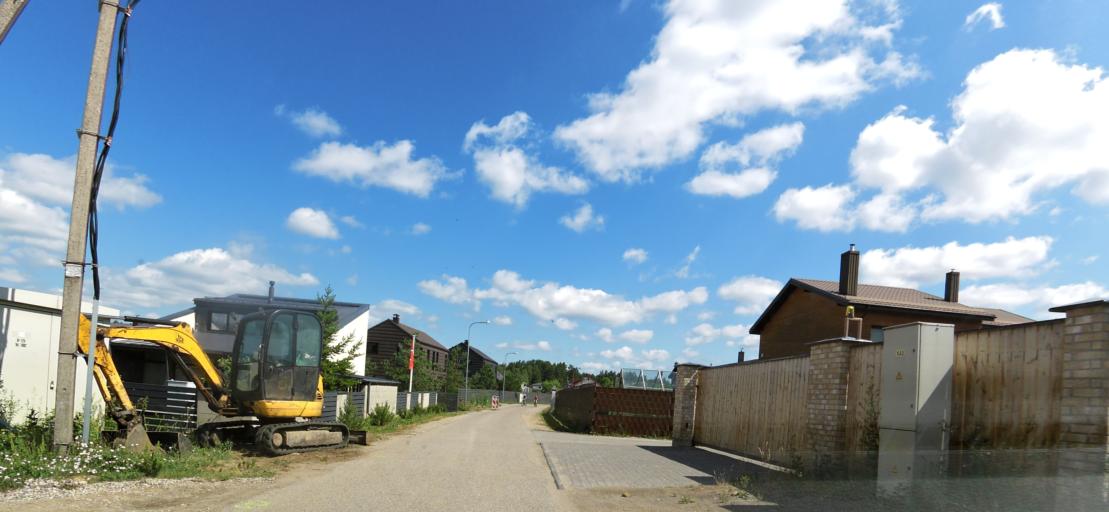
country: LT
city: Nemencine
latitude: 54.8206
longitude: 25.3945
